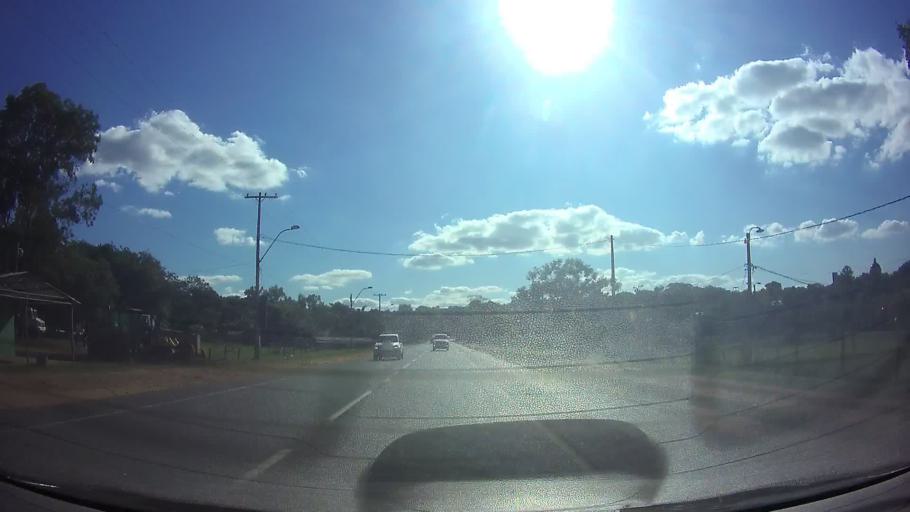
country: PY
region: Cordillera
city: Caacupe
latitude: -25.3890
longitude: -57.1356
